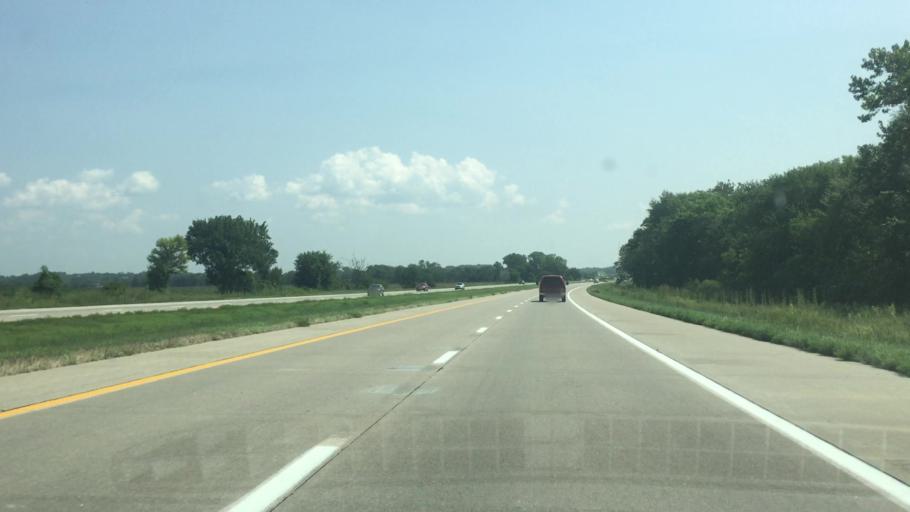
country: US
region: Kansas
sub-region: Franklin County
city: Ottawa
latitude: 38.5551
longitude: -95.3457
